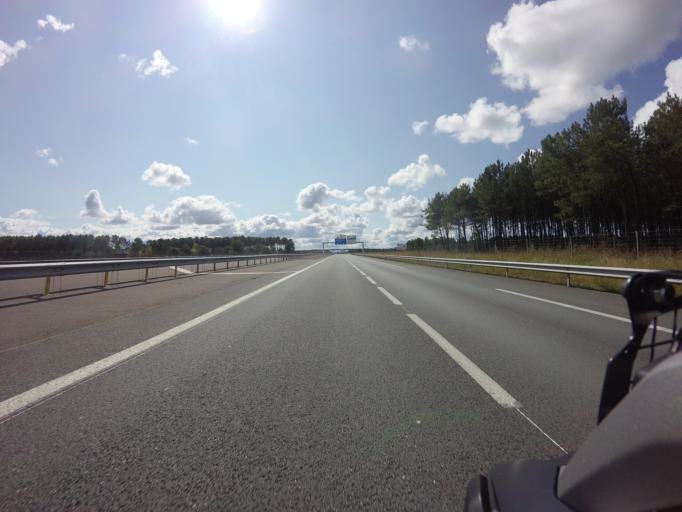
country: FR
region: Aquitaine
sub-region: Departement des Landes
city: Saint-Geours-de-Maremne
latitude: 43.7156
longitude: -1.2280
